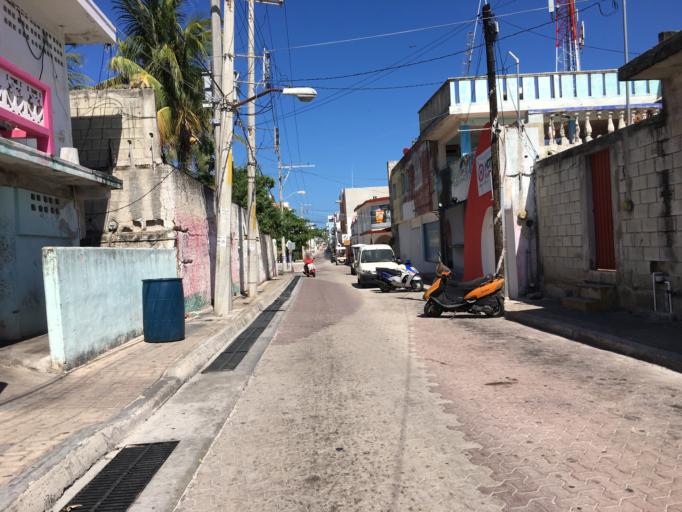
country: MX
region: Quintana Roo
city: Isla Mujeres
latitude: 21.2582
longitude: -86.7481
